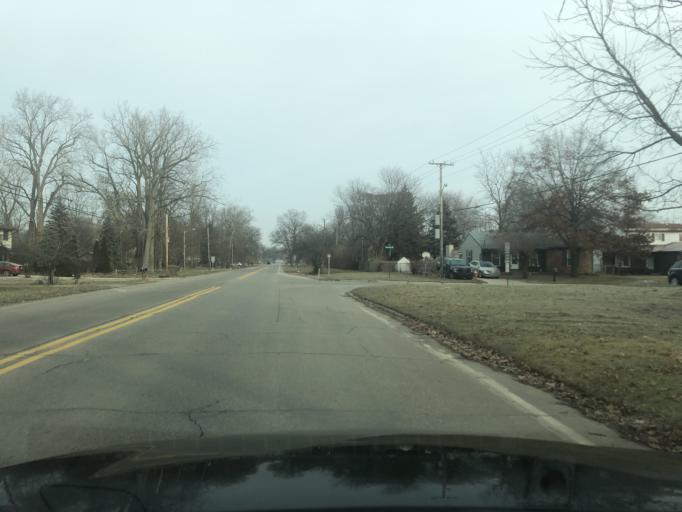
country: US
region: Michigan
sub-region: Wayne County
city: Taylor
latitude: 42.1846
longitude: -83.3256
